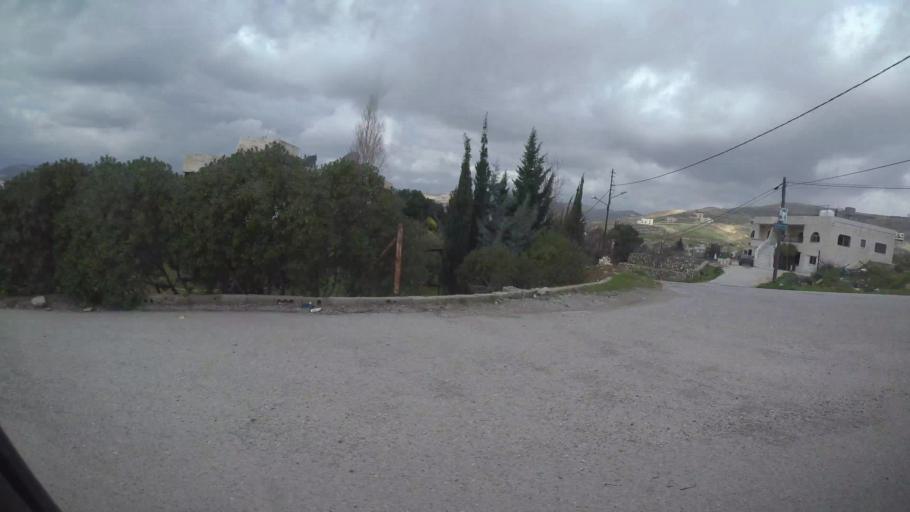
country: JO
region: Amman
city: Al Jubayhah
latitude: 32.0750
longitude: 35.8673
